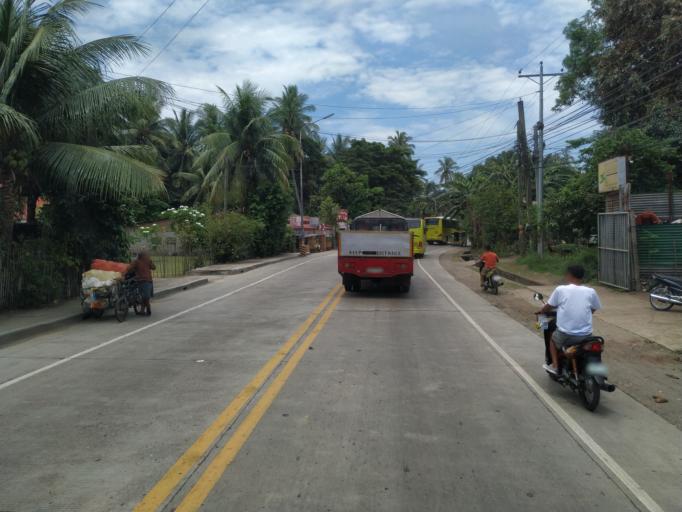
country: PH
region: Central Visayas
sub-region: Province of Negros Oriental
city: Sibulan
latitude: 9.3521
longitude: 123.2847
